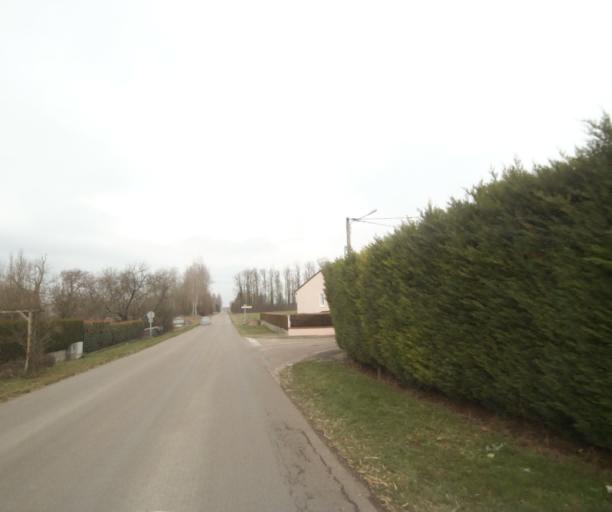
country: FR
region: Champagne-Ardenne
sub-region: Departement de la Haute-Marne
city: Villiers-en-Lieu
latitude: 48.6697
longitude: 4.8935
